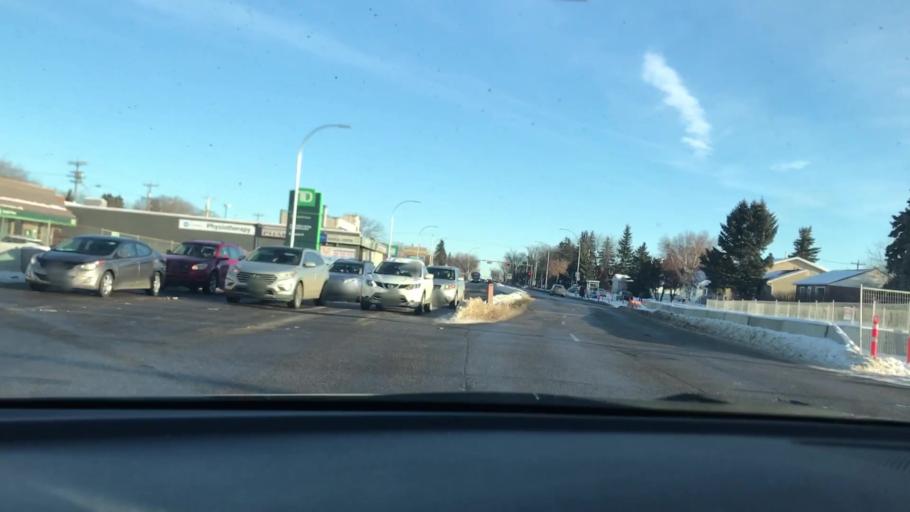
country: CA
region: Alberta
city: Edmonton
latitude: 53.5181
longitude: -113.4555
